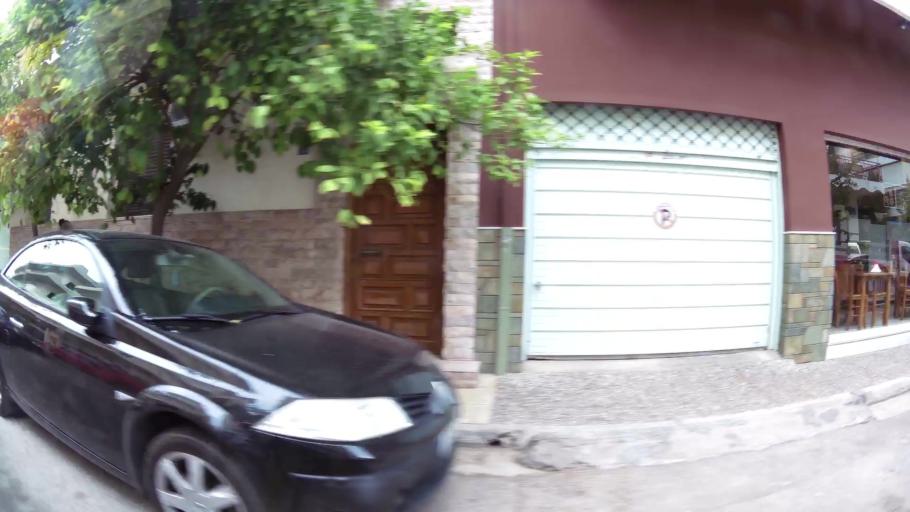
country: GR
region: Attica
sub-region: Nomarchia Athinas
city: Agia Varvara
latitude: 37.9846
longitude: 23.6698
